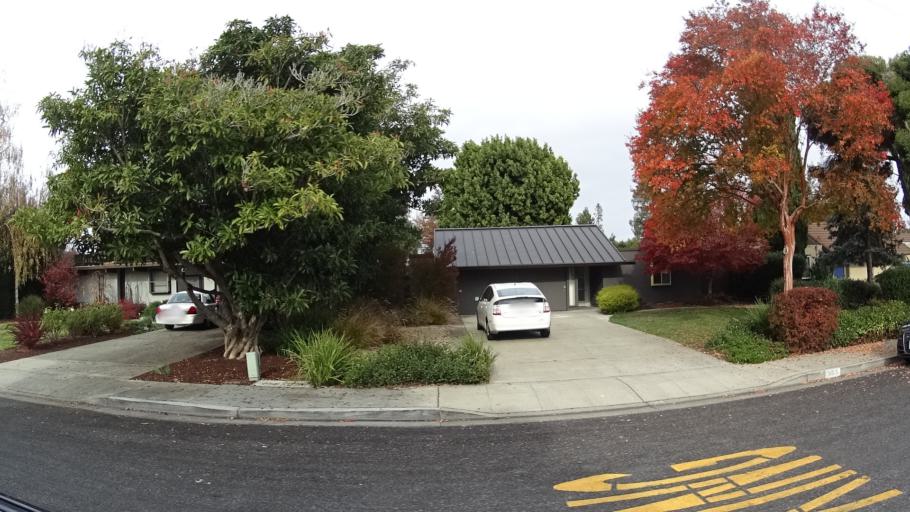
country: US
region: California
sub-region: Santa Clara County
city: Sunnyvale
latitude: 37.3677
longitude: -122.0446
